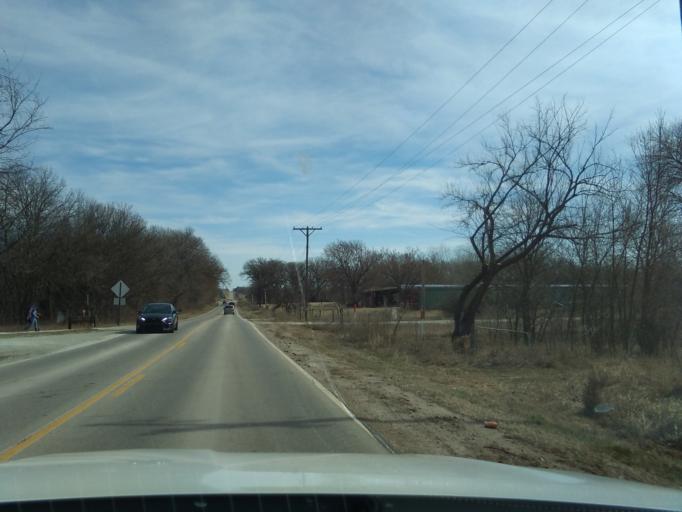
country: US
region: Nebraska
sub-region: Lancaster County
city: Hickman
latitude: 40.6974
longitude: -96.6890
